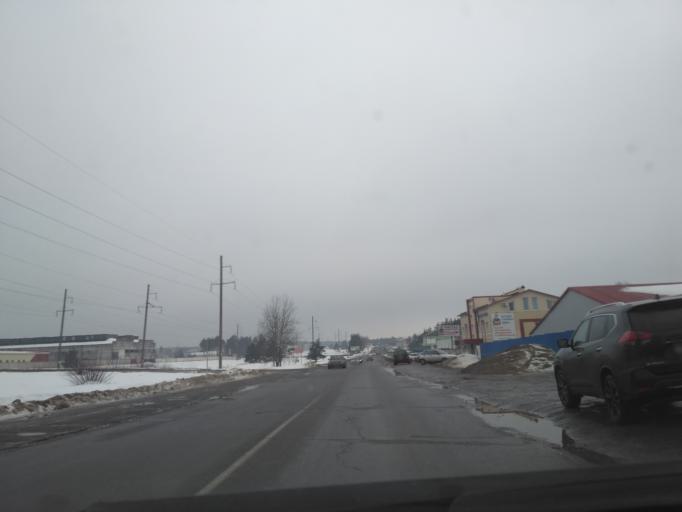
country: BY
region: Minsk
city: Horad Barysaw
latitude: 54.1988
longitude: 28.5026
